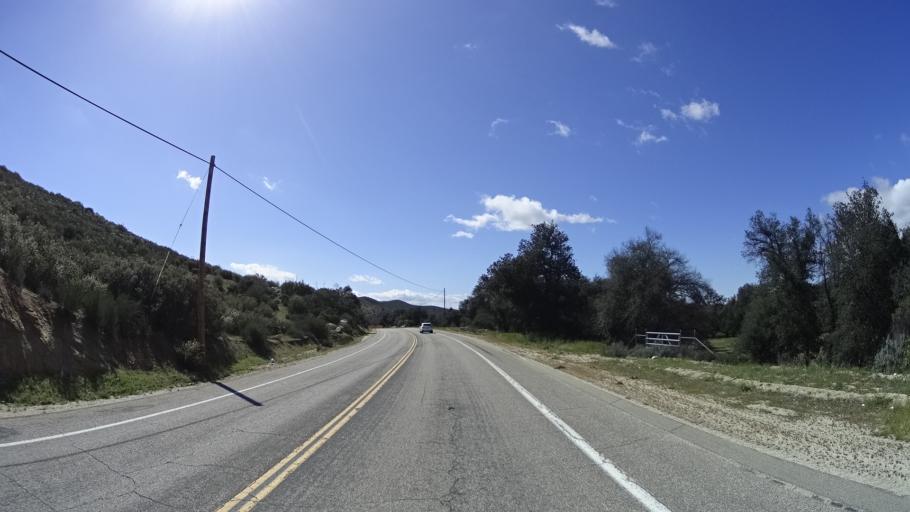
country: US
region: California
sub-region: San Diego County
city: Julian
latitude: 33.2134
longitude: -116.5558
